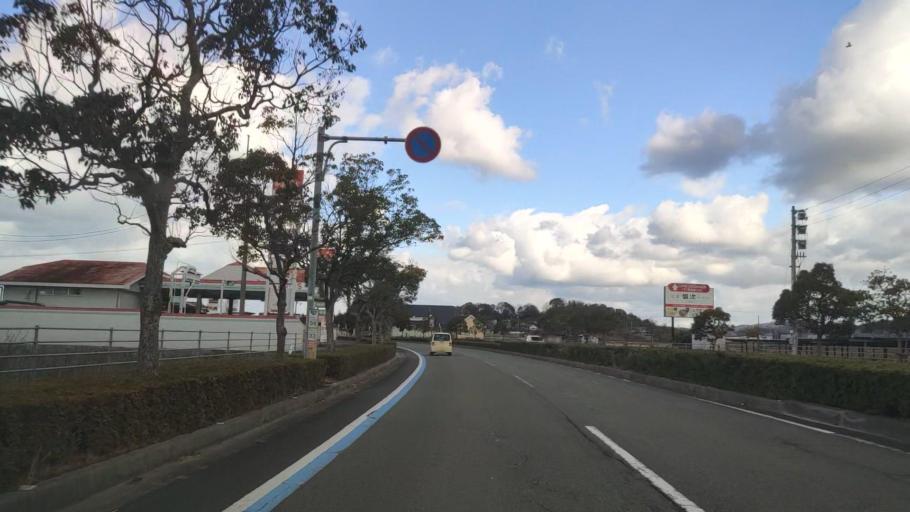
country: JP
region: Ehime
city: Hojo
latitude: 33.9437
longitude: 132.7758
